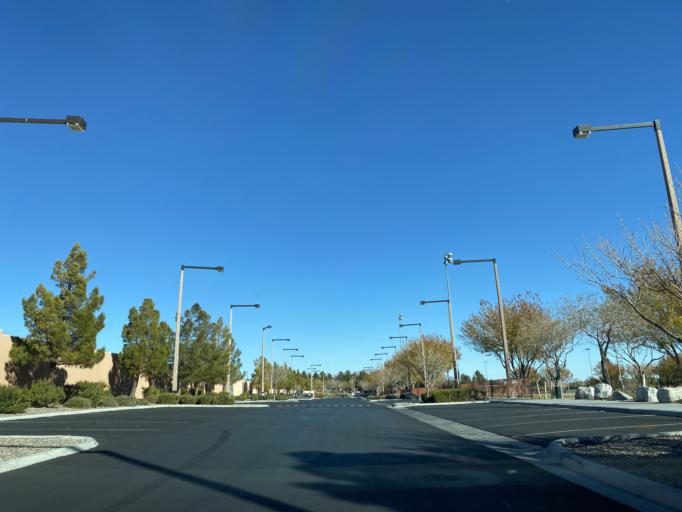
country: US
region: Nevada
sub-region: Clark County
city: Summerlin South
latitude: 36.1690
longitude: -115.3467
